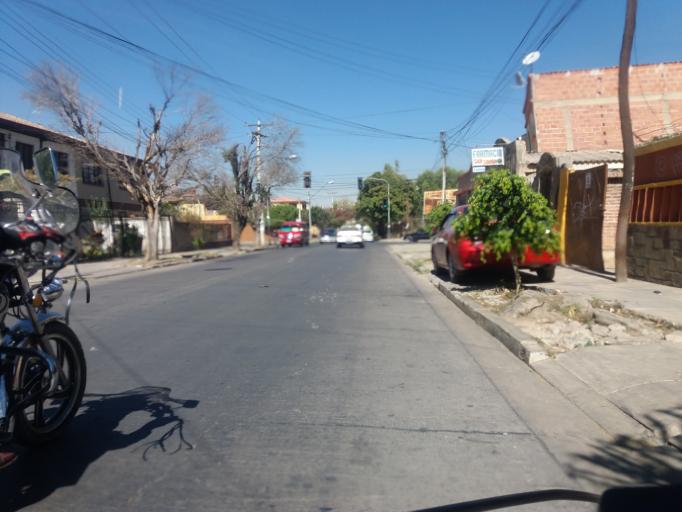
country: BO
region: Cochabamba
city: Cochabamba
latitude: -17.3914
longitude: -66.1430
